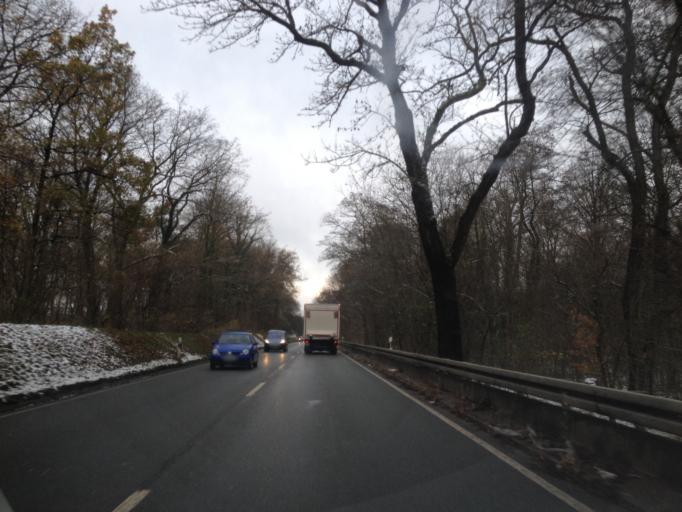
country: DE
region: Bavaria
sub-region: Regierungsbezirk Mittelfranken
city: Schwaig
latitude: 49.4730
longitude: 11.1470
